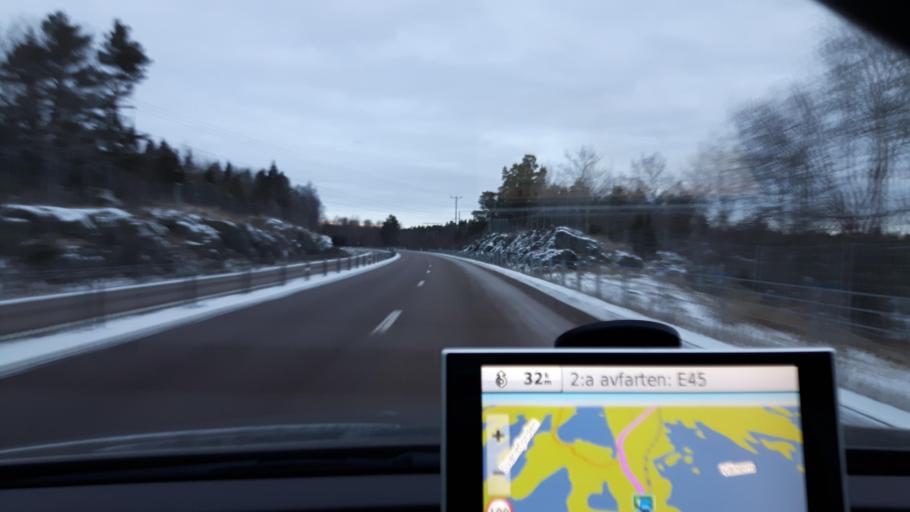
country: SE
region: Vaestra Goetaland
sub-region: Melleruds Kommun
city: Mellerud
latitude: 58.8023
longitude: 12.5264
